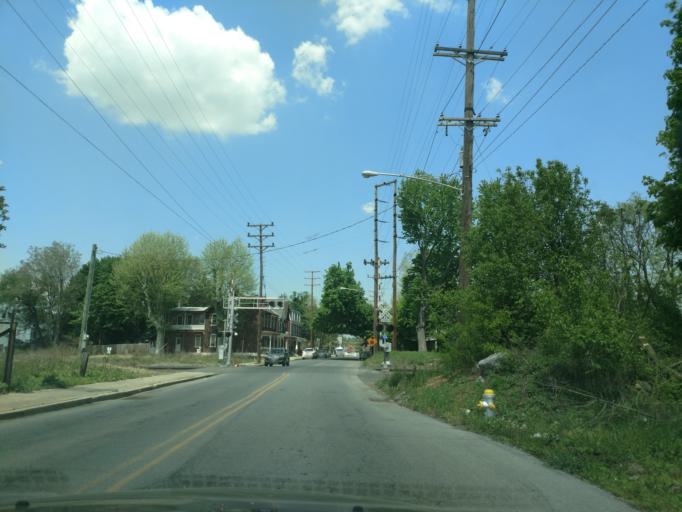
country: US
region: Pennsylvania
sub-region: Lebanon County
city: Hebron
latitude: 40.3444
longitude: -76.4041
